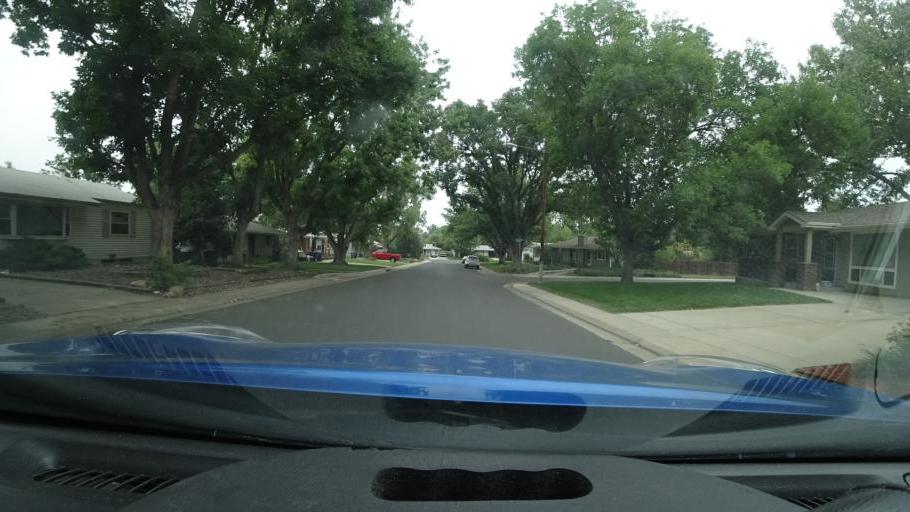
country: US
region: Colorado
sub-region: Arapahoe County
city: Glendale
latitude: 39.6922
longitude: -104.9193
